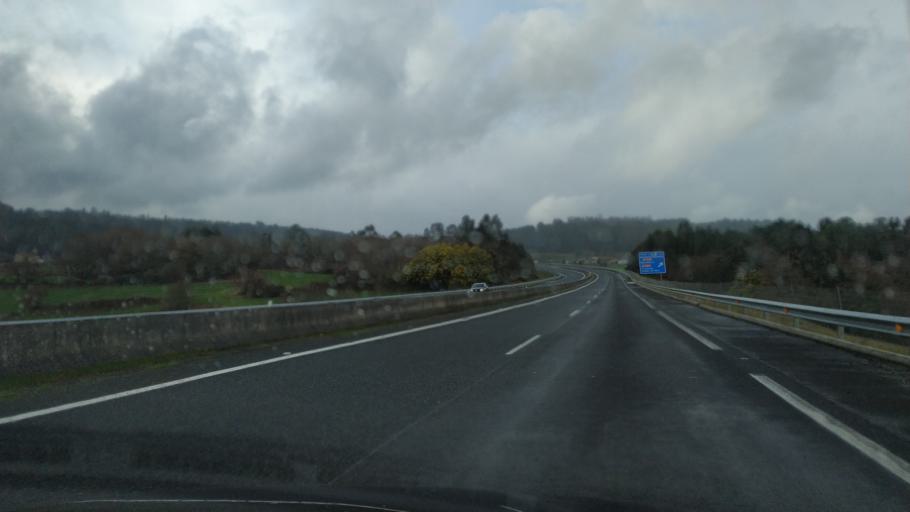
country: ES
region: Galicia
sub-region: Provincia de Pontevedra
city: Silleda
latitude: 42.7267
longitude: -8.3228
